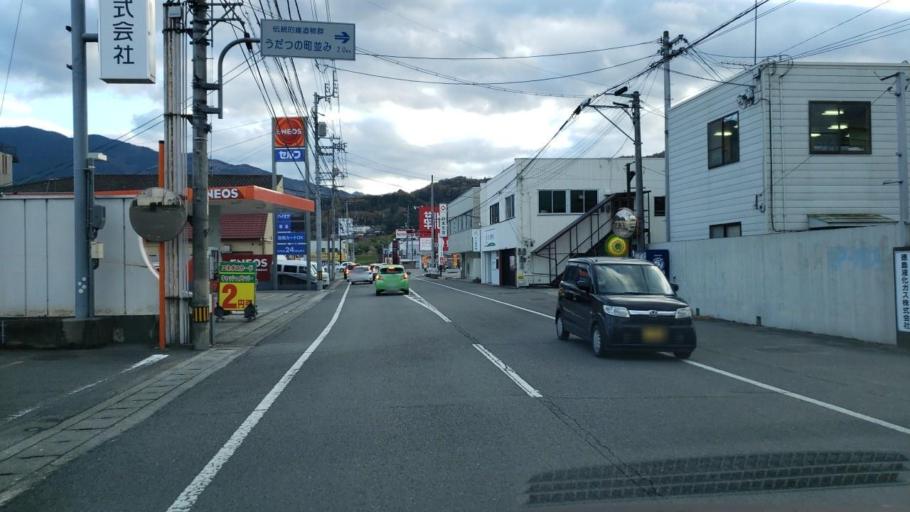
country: JP
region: Tokushima
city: Wakimachi
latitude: 34.0646
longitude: 134.1635
